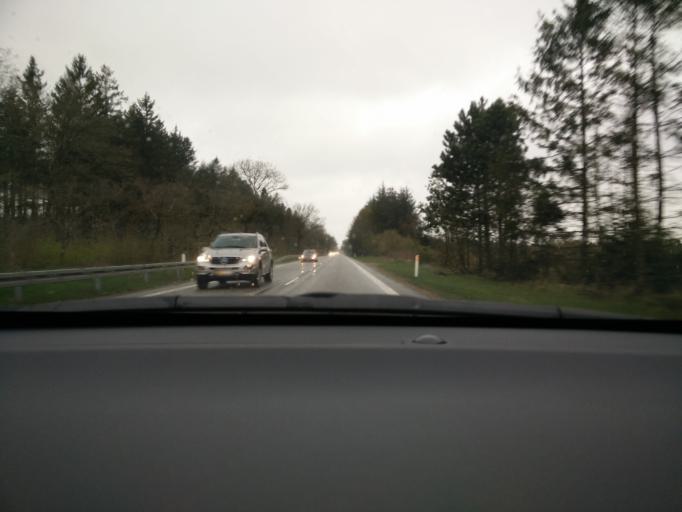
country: DK
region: Central Jutland
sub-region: Viborg Kommune
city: Stoholm
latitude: 56.5248
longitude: 9.2309
